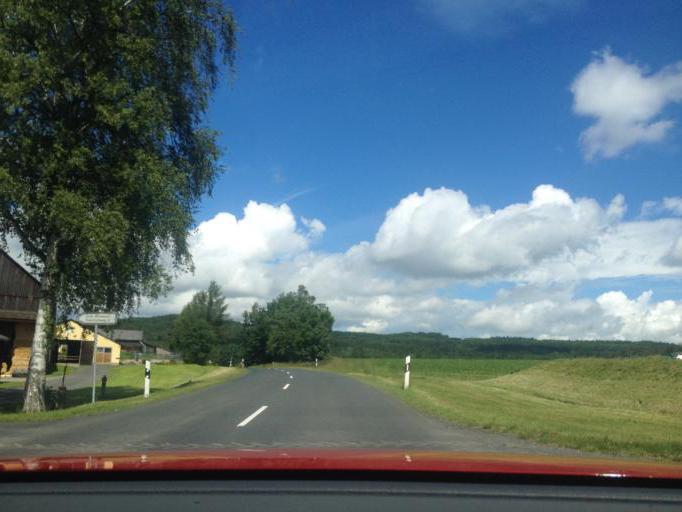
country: DE
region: Bavaria
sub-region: Upper Palatinate
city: Pechbrunn
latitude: 49.9772
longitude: 12.1772
